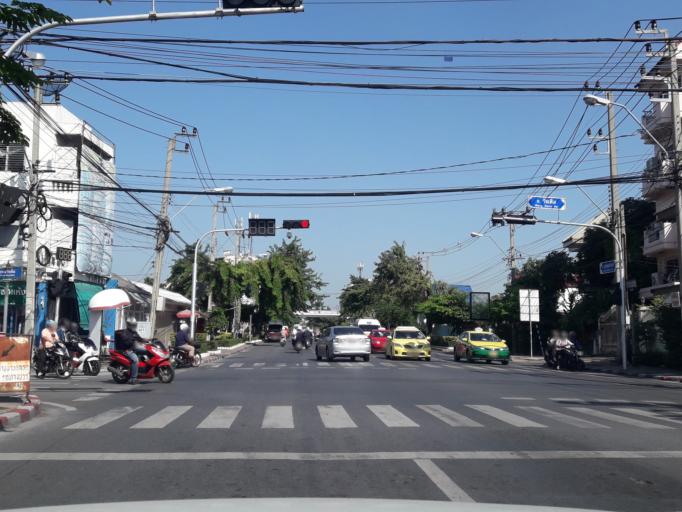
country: TH
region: Bangkok
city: Thon Buri
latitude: 13.7420
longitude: 100.4876
